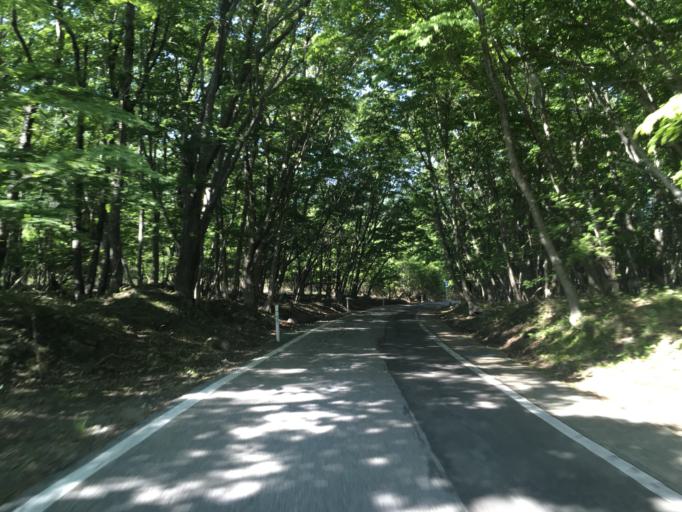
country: JP
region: Iwate
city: Ofunato
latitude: 39.1841
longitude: 141.7661
